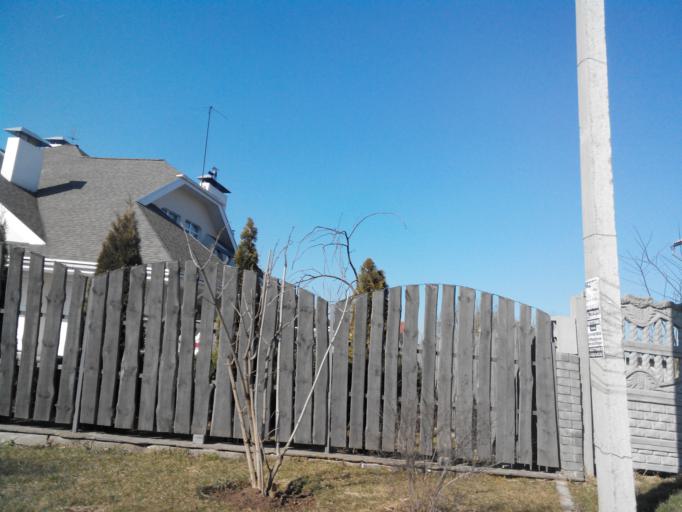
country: BY
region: Minsk
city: Zhdanovichy
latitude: 53.9212
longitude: 27.4055
